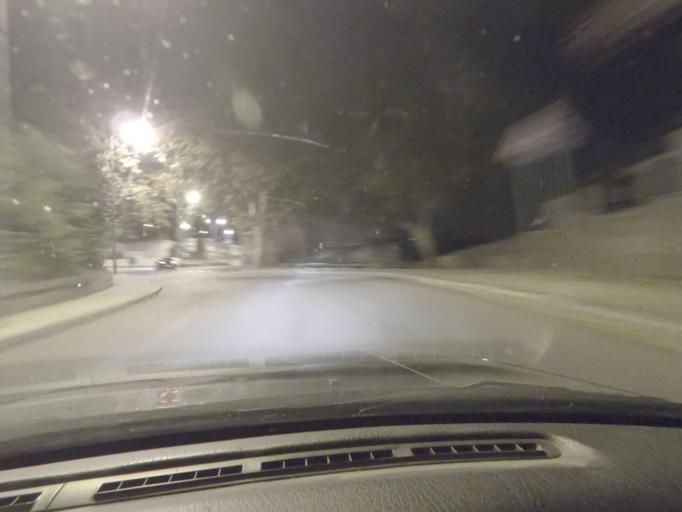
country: PT
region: Vila Real
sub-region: Peso da Regua
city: Peso da Regua
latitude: 41.1654
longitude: -7.7931
